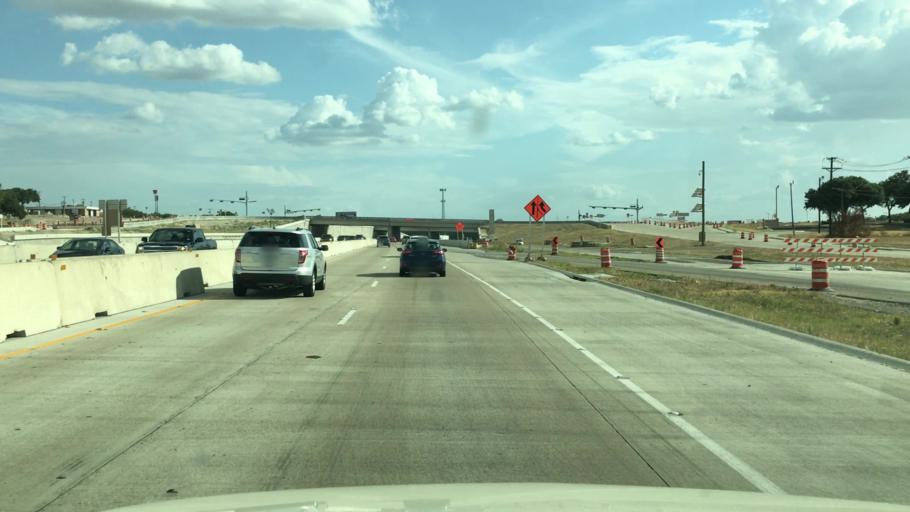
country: US
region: Texas
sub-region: Bell County
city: Temple
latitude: 31.1057
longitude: -97.3587
